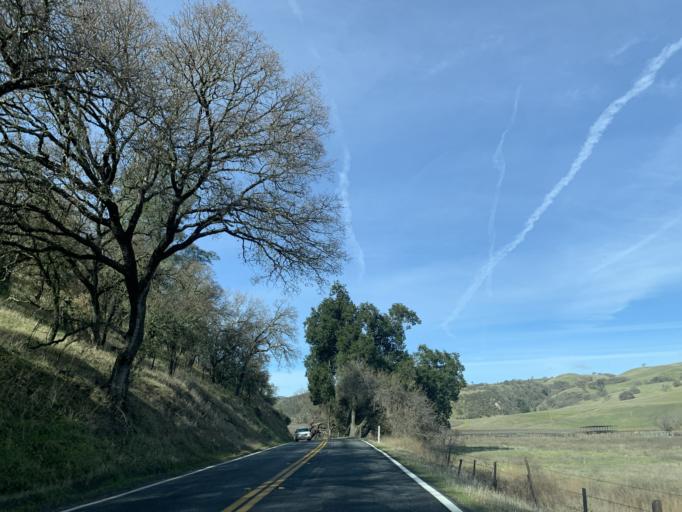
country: US
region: California
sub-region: Monterey County
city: Soledad
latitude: 36.5109
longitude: -121.1155
